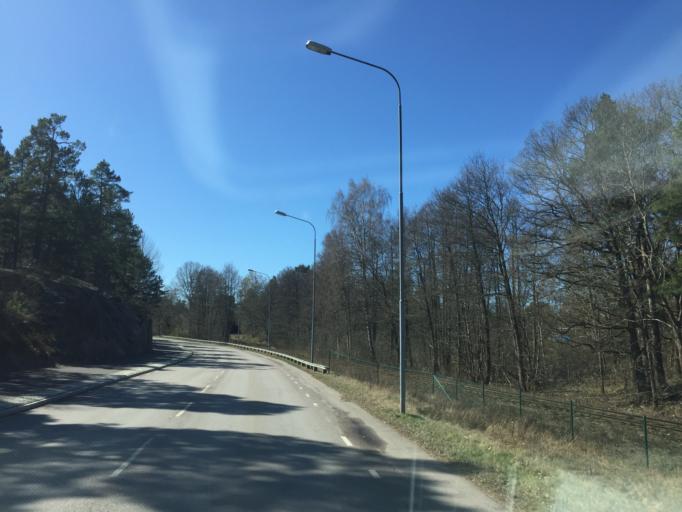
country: SE
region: Kalmar
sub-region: Oskarshamns Kommun
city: Oskarshamn
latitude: 57.2535
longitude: 16.4619
